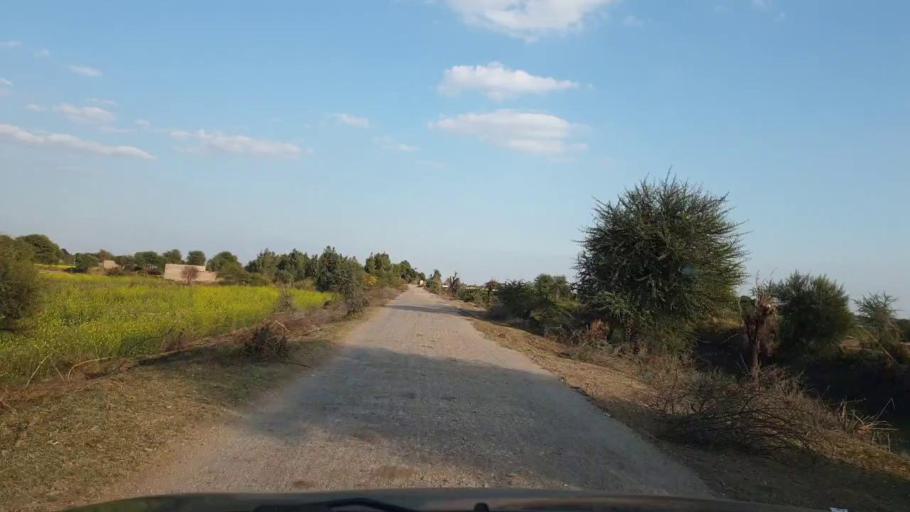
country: PK
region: Sindh
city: Sinjhoro
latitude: 25.9947
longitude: 68.7510
